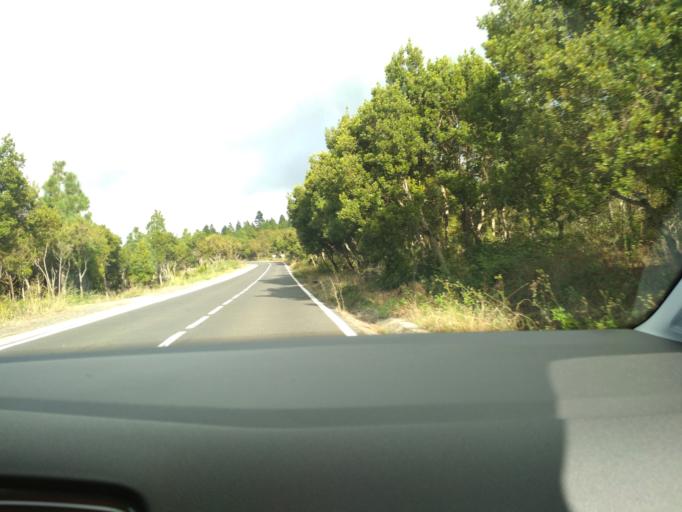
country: ES
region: Canary Islands
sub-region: Provincia de Santa Cruz de Tenerife
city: Garachico
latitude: 28.3291
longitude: -16.7794
